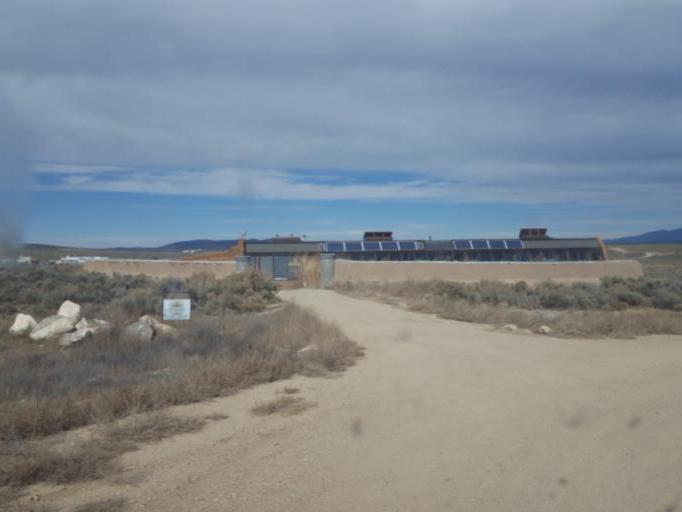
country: US
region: New Mexico
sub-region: Taos County
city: Arroyo Seco
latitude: 36.4964
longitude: -105.7525
